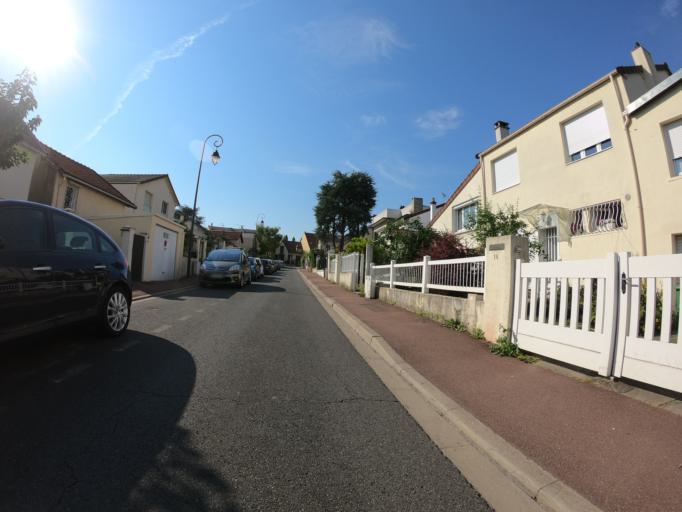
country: FR
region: Ile-de-France
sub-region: Departement des Hauts-de-Seine
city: Antony
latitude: 48.7440
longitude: 2.2947
